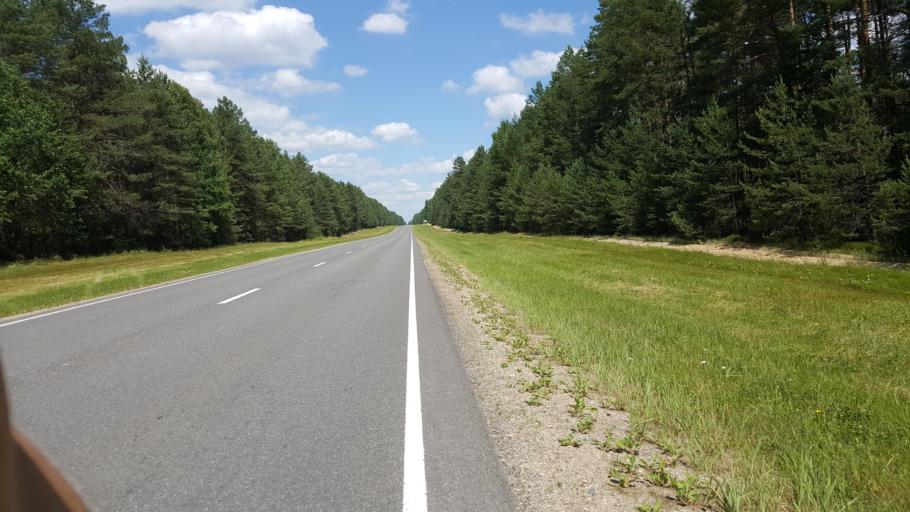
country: BY
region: Brest
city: Kamyanyuki
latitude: 52.5178
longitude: 23.7896
